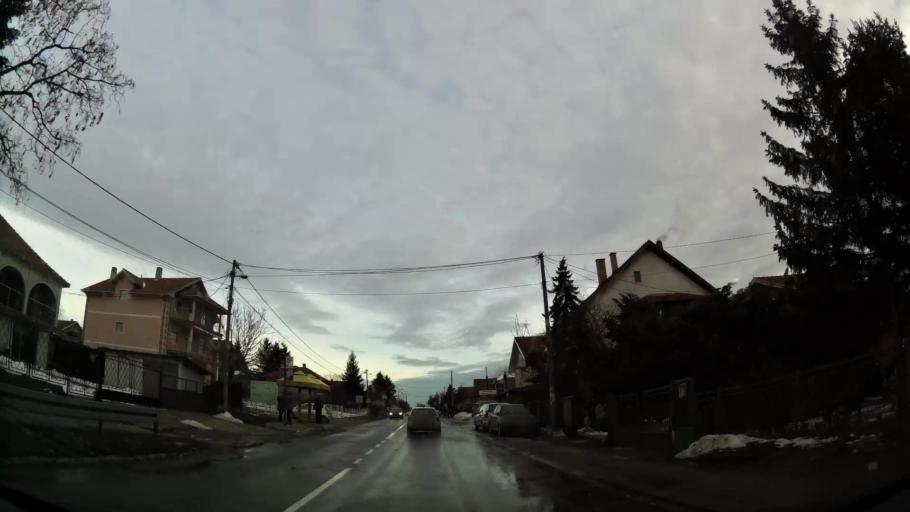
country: RS
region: Central Serbia
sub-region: Belgrade
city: Rakovica
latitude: 44.7220
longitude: 20.4972
